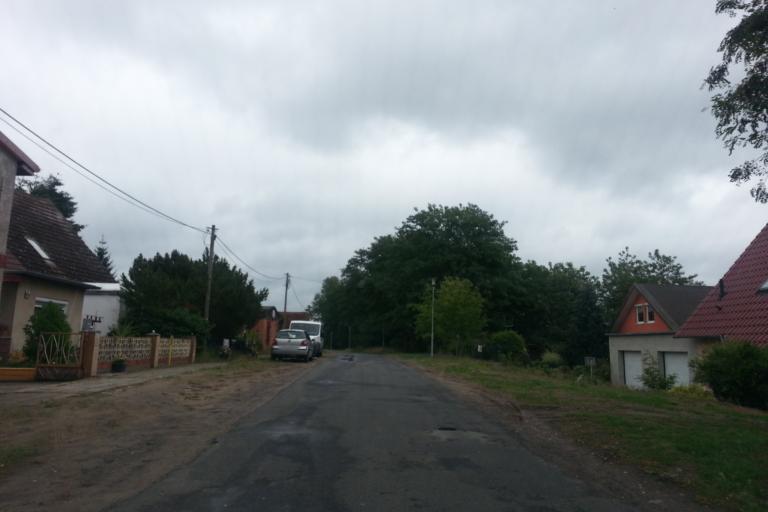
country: DE
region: Mecklenburg-Vorpommern
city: Ferdinandshof
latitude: 53.6576
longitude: 13.9240
